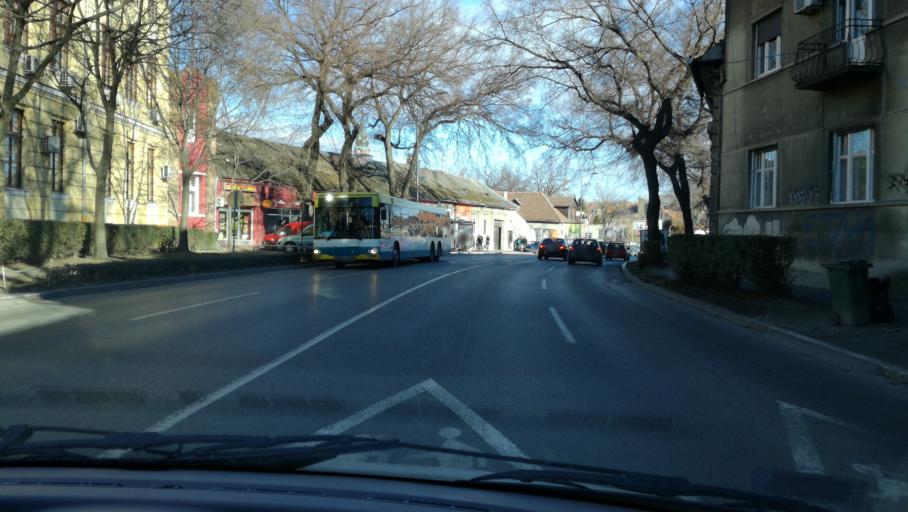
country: RS
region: Autonomna Pokrajina Vojvodina
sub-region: Severnobacki Okrug
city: Subotica
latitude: 46.0961
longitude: 19.6615
